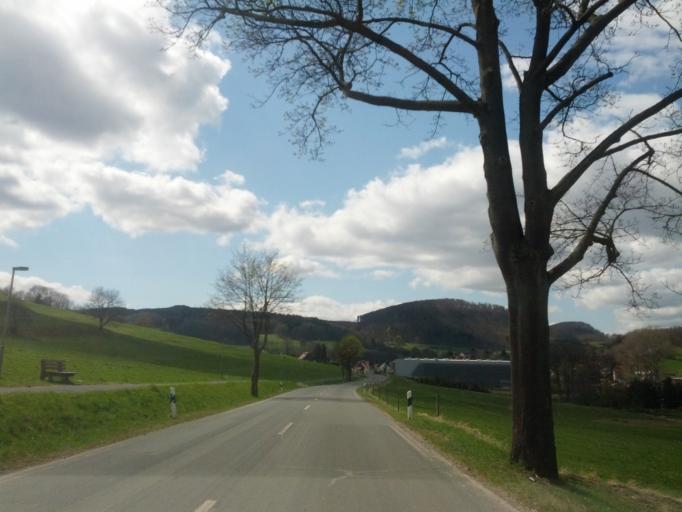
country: DE
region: Thuringia
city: Seebach
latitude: 50.9024
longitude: 10.4611
